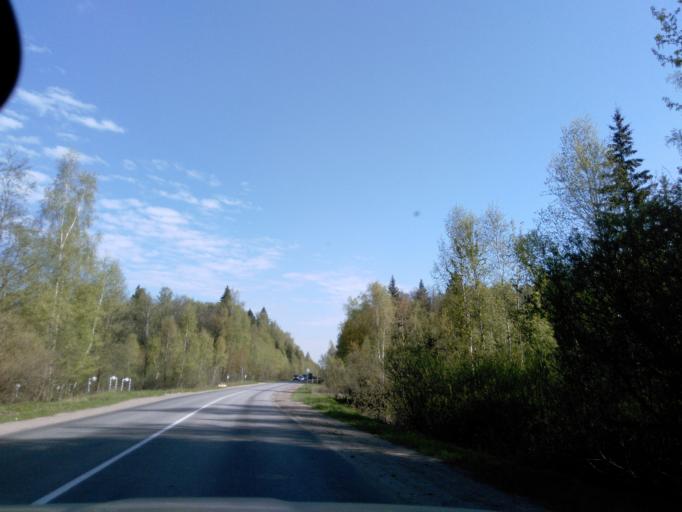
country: RU
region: Moskovskaya
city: Mendeleyevo
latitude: 56.0211
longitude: 37.2073
